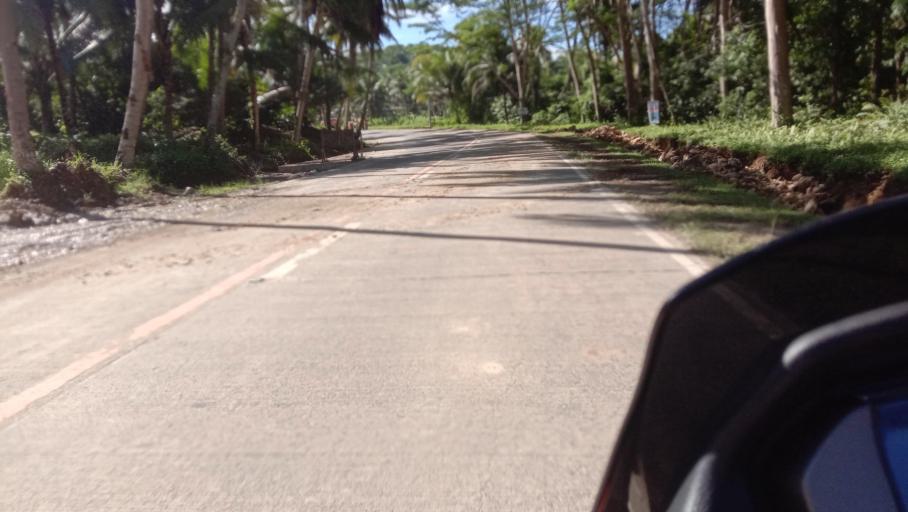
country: PH
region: Caraga
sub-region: Province of Surigao del Sur
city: Barobo
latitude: 8.5375
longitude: 126.0981
